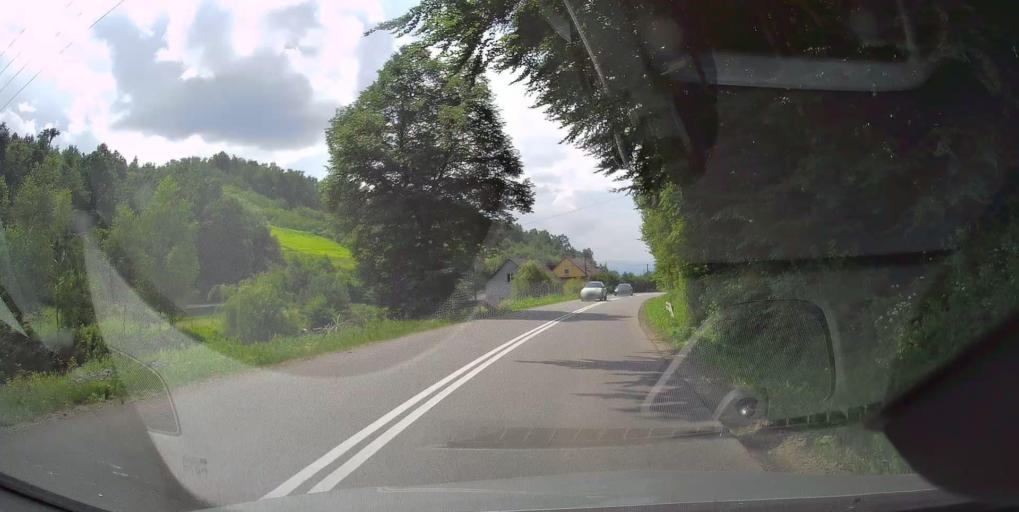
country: PL
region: Lesser Poland Voivodeship
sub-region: Powiat nowosadecki
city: Nowy Sacz
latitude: 49.6488
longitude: 20.7214
